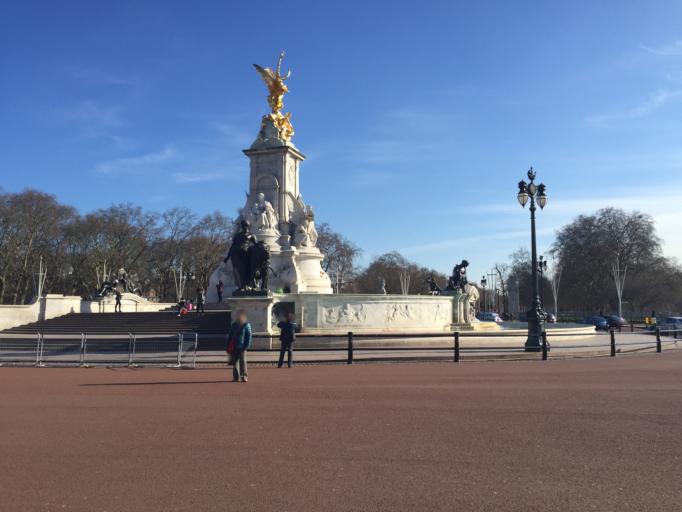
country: GB
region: England
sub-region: Greater London
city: London
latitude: 51.5014
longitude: -0.1410
